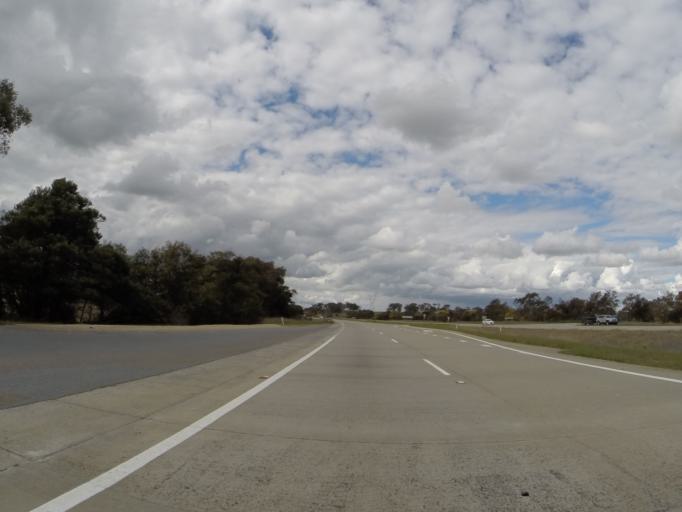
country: AU
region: New South Wales
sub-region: Yass Valley
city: Gundaroo
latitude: -34.8224
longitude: 149.3996
